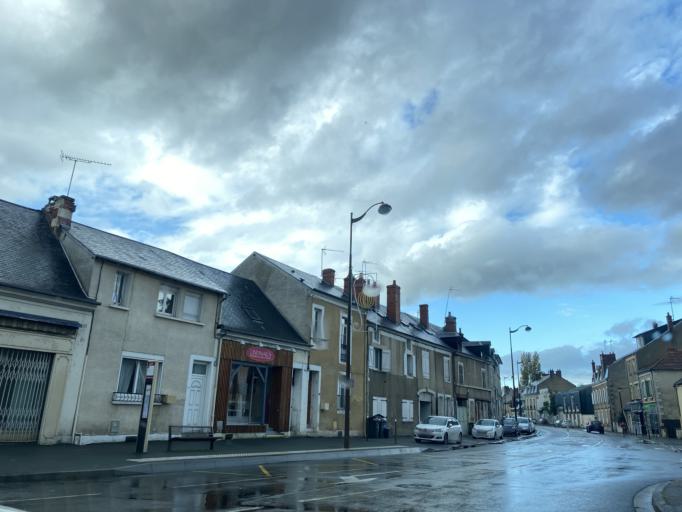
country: FR
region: Centre
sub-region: Departement du Cher
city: Bourges
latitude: 47.0770
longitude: 2.3901
